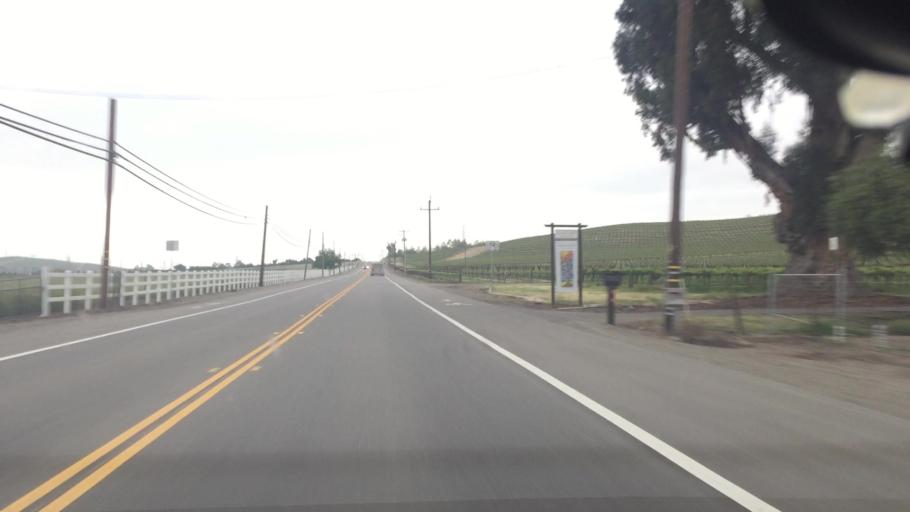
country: US
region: California
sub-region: Alameda County
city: Livermore
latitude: 37.6651
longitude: -121.7056
